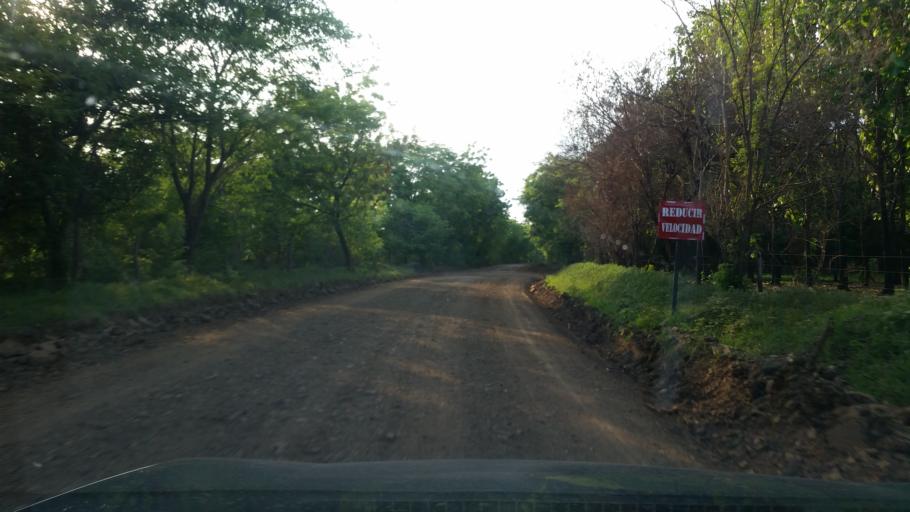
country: NI
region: Managua
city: Masachapa
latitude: 11.7718
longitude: -86.4927
